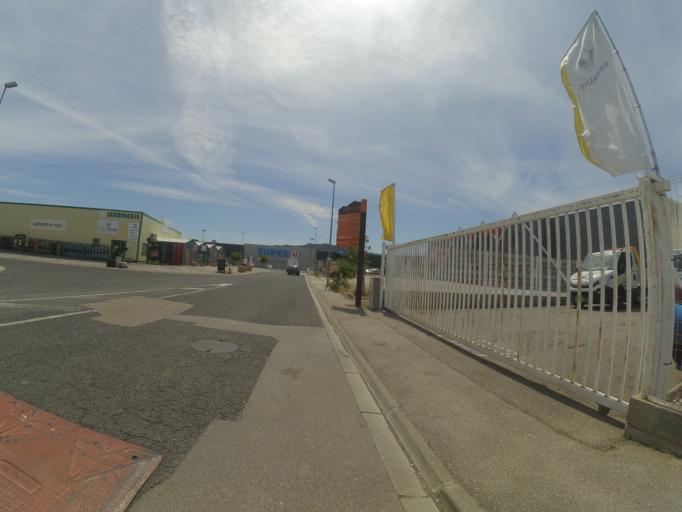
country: FR
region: Languedoc-Roussillon
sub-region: Departement des Pyrenees-Orientales
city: Ille-sur-Tet
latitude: 42.6772
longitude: 2.6329
